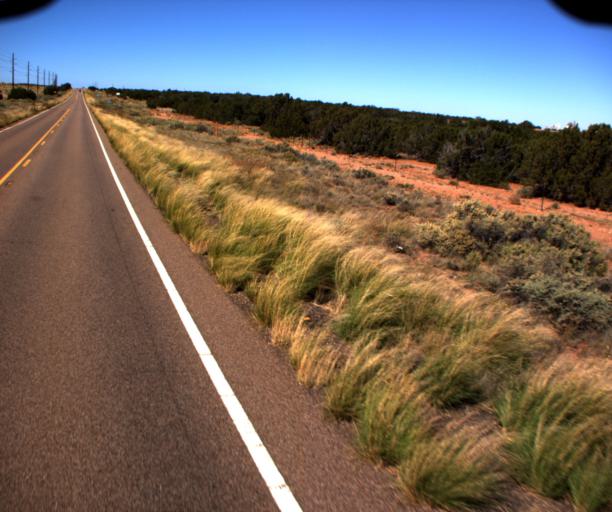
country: US
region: Arizona
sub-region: Navajo County
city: Taylor
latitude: 34.4828
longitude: -110.3088
